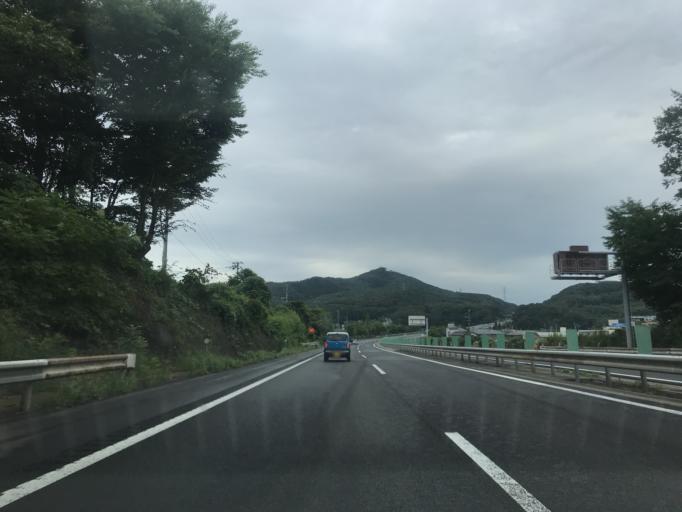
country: JP
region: Miyagi
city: Sendai
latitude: 38.2619
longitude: 140.8102
